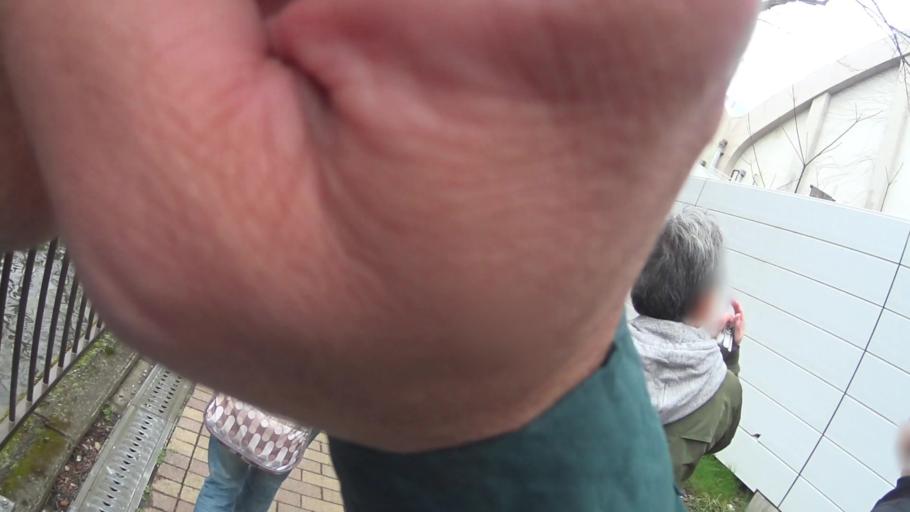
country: JP
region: Tokyo
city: Chofugaoka
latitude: 35.6355
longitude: 139.6044
